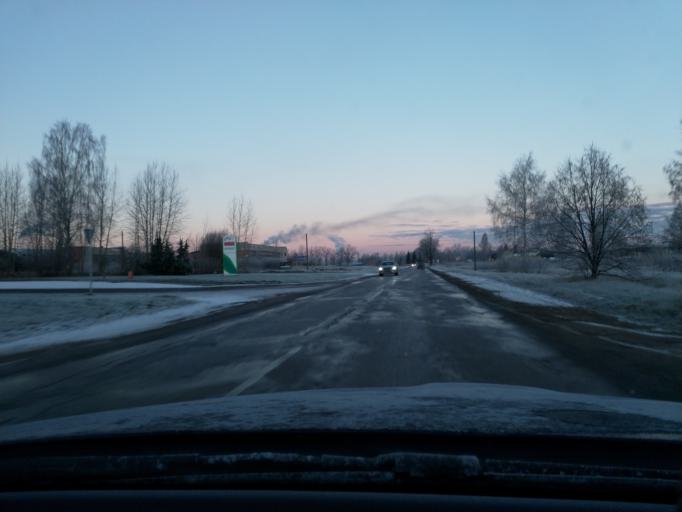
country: LV
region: Kuldigas Rajons
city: Kuldiga
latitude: 56.9538
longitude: 21.9924
